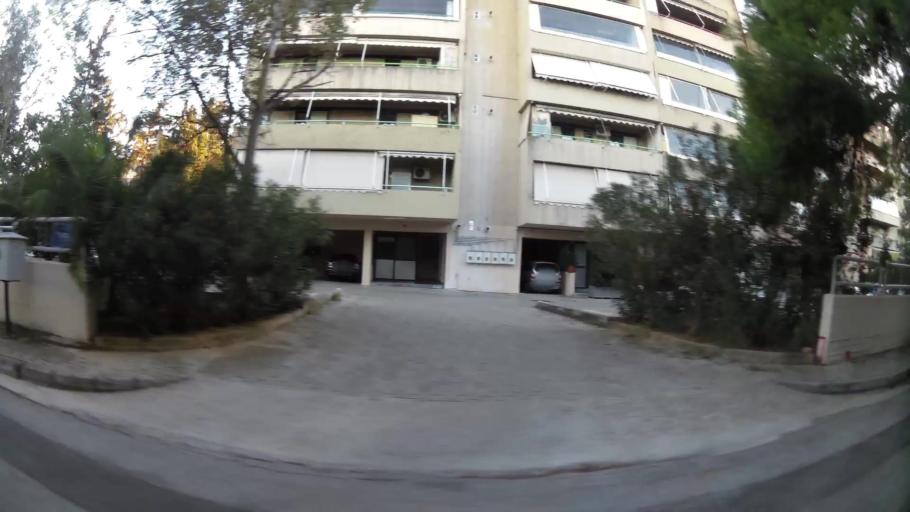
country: GR
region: Attica
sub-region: Nomarchia Athinas
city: Lykovrysi
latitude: 38.0691
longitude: 23.7916
